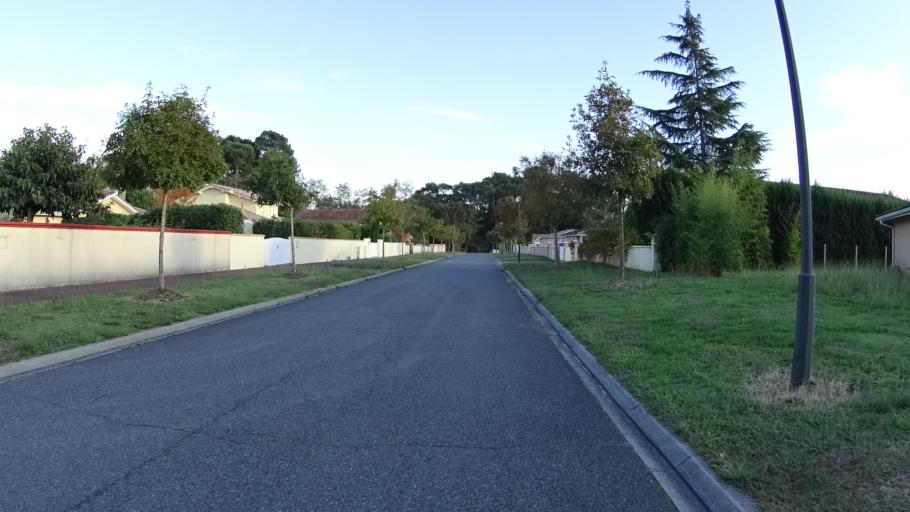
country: FR
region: Aquitaine
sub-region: Departement des Landes
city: Saint-Paul-les-Dax
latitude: 43.7355
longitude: -1.0456
